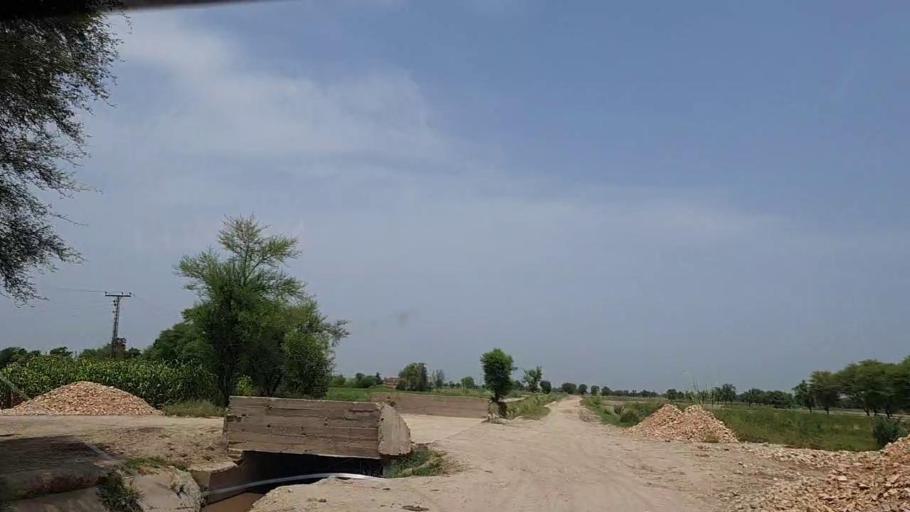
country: PK
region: Sindh
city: Tharu Shah
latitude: 26.9372
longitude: 68.0682
